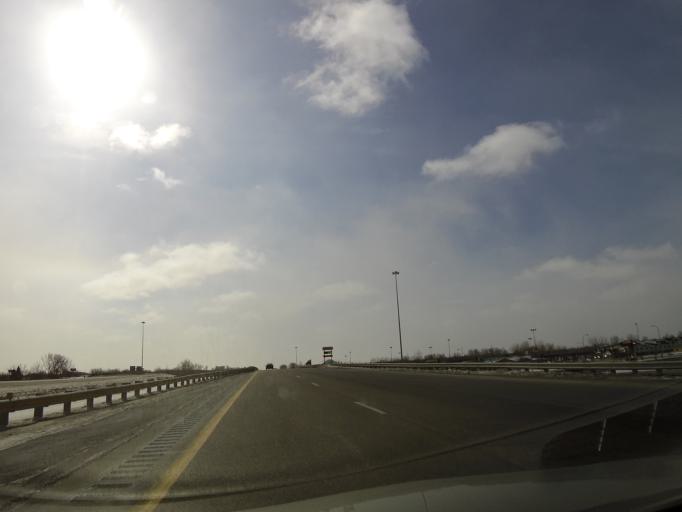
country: US
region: North Dakota
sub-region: Grand Forks County
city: Grand Forks
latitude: 47.9344
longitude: -97.0937
